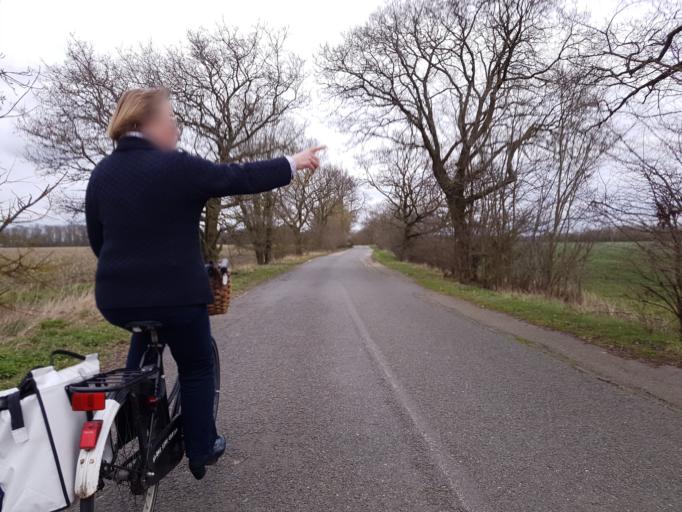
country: GB
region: England
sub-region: Cambridgeshire
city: Girton
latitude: 52.2304
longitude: 0.0460
